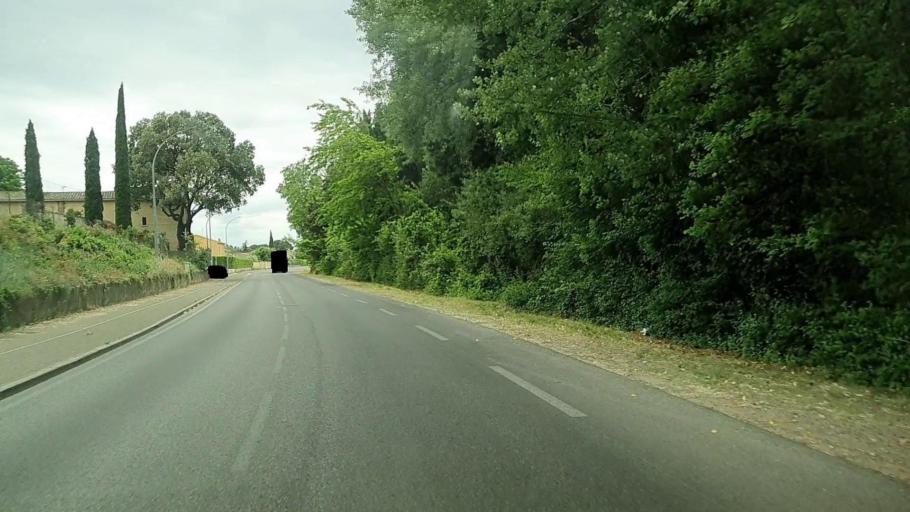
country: FR
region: Languedoc-Roussillon
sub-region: Departement du Gard
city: Bagnols-sur-Ceze
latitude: 44.1446
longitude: 4.6103
